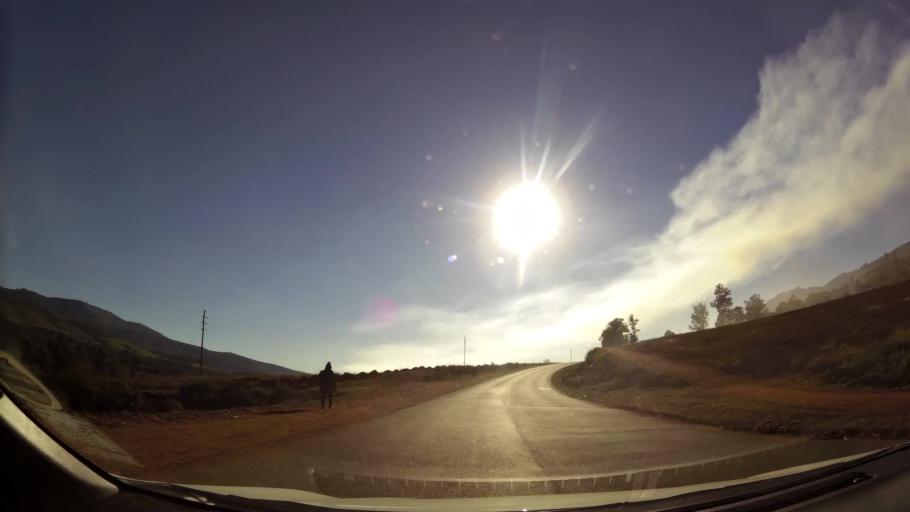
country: ZA
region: Limpopo
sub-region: Mopani District Municipality
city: Tzaneen
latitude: -23.9051
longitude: 30.0631
